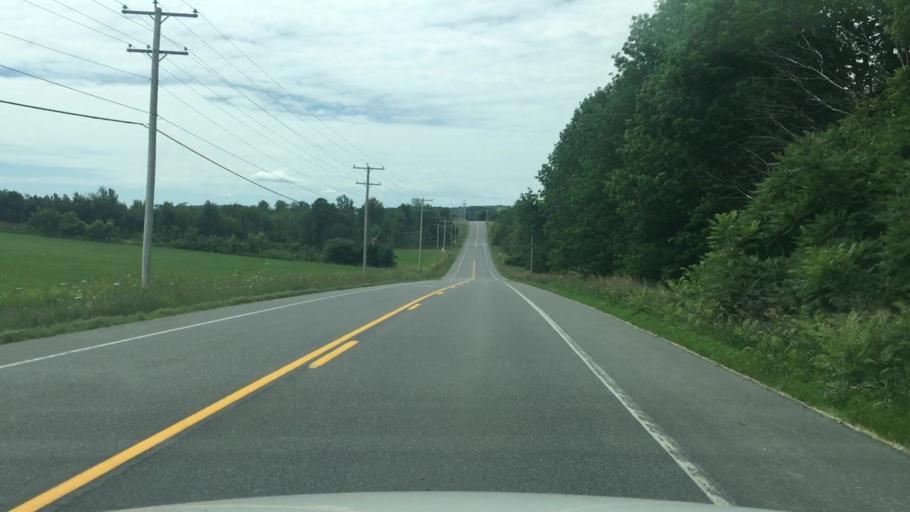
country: US
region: Maine
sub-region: Waldo County
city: Troy
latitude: 44.5394
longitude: -69.2667
